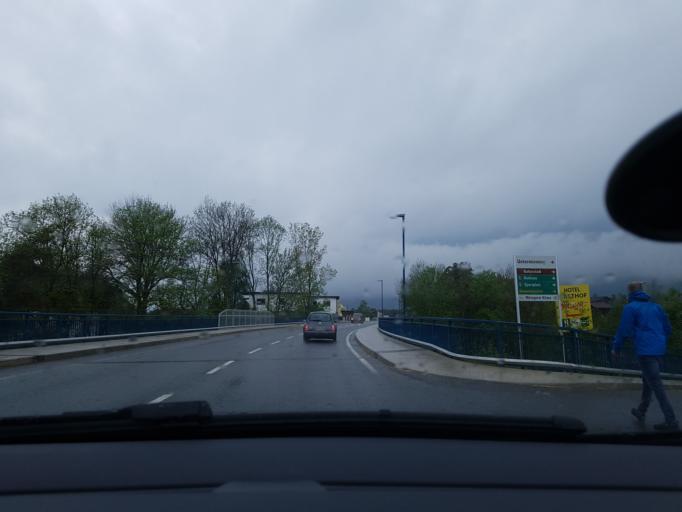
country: AT
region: Tyrol
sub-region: Politischer Bezirk Imst
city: Mieming
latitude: 47.3046
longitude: 10.9836
